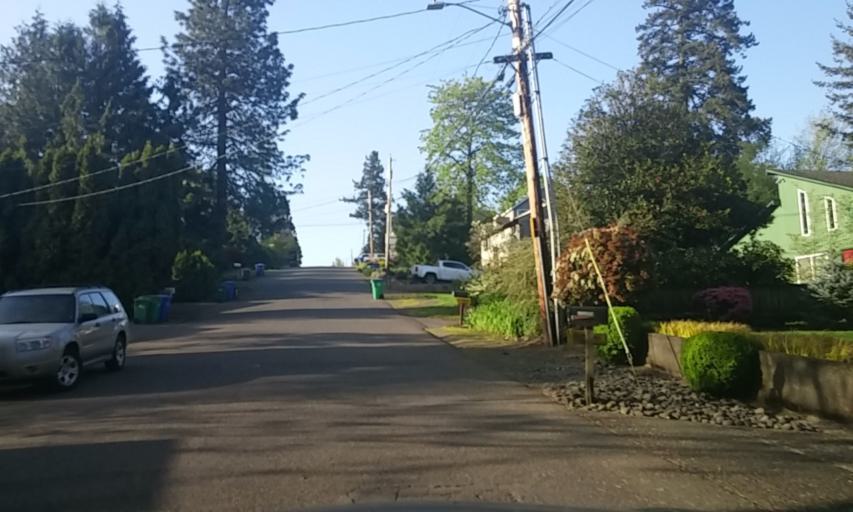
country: US
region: Oregon
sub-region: Washington County
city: Metzger
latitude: 45.4462
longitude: -122.7427
